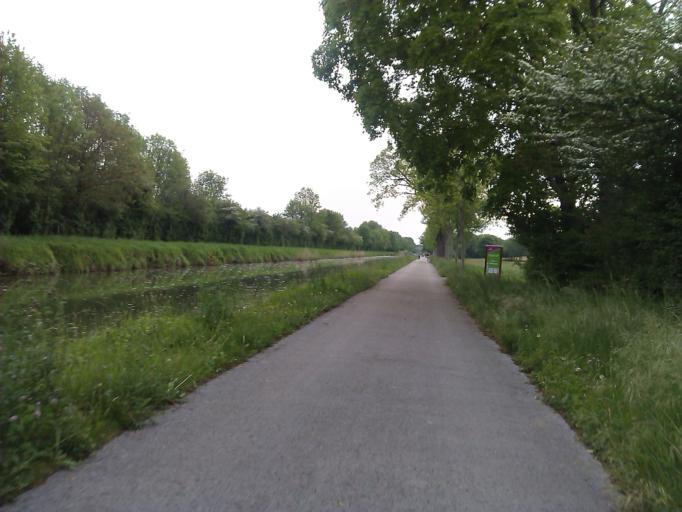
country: FR
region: Franche-Comte
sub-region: Departement du Jura
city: Fraisans
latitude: 47.1566
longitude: 5.7566
